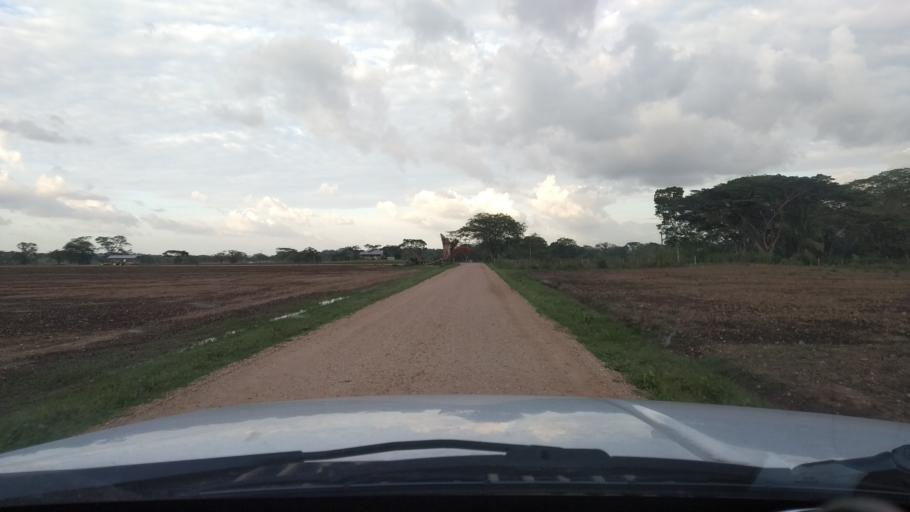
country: BZ
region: Cayo
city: San Ignacio
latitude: 17.2171
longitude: -89.0007
